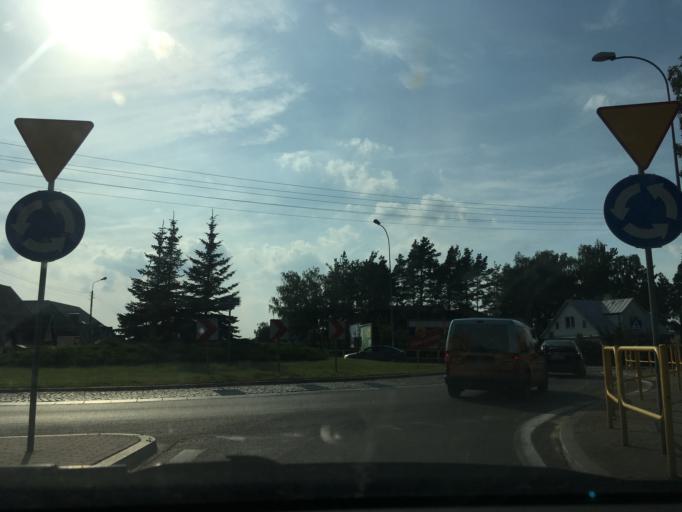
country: PL
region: Podlasie
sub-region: Powiat bialostocki
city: Wasilkow
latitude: 53.1253
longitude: 23.2596
